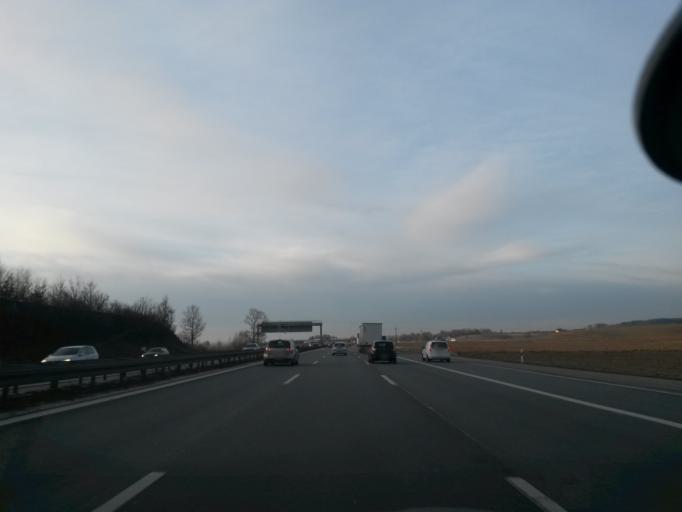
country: DE
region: Bavaria
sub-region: Upper Bavaria
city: Allershausen
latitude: 48.4222
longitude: 11.5894
